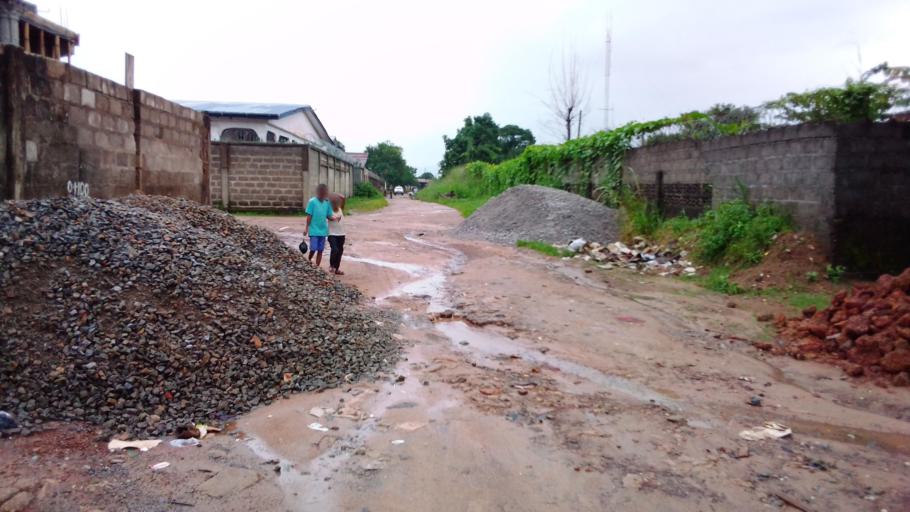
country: SL
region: Eastern Province
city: Kenema
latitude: 7.8895
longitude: -11.1881
